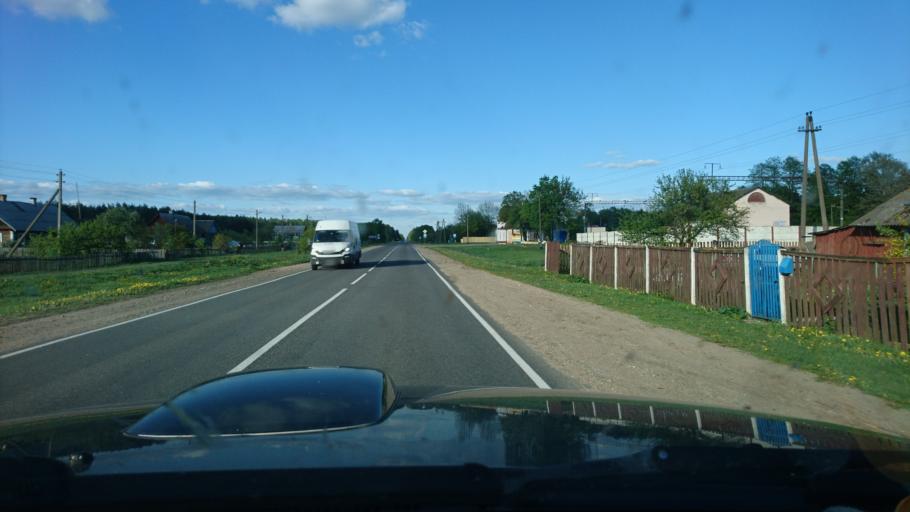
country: BY
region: Brest
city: Nyakhachava
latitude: 52.6506
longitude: 25.2190
